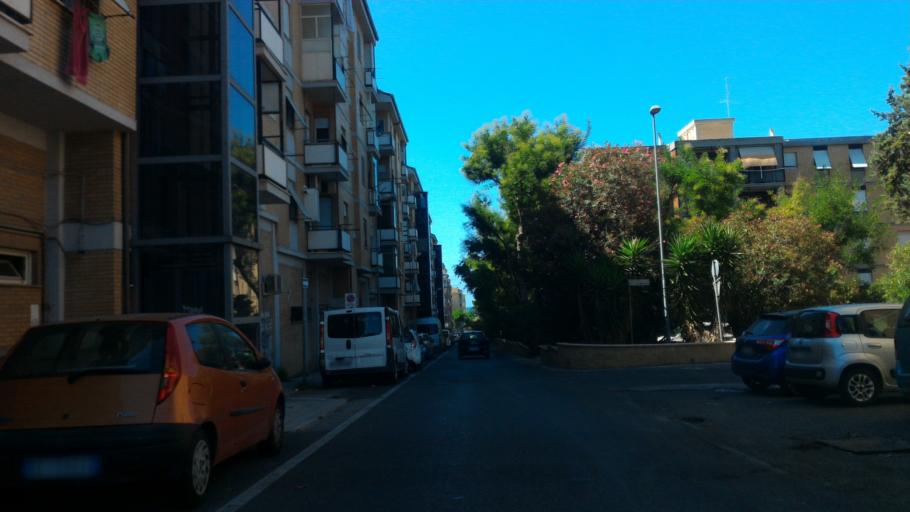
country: IT
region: Latium
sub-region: Citta metropolitana di Roma Capitale
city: Civitavecchia
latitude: 42.0831
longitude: 11.8125
